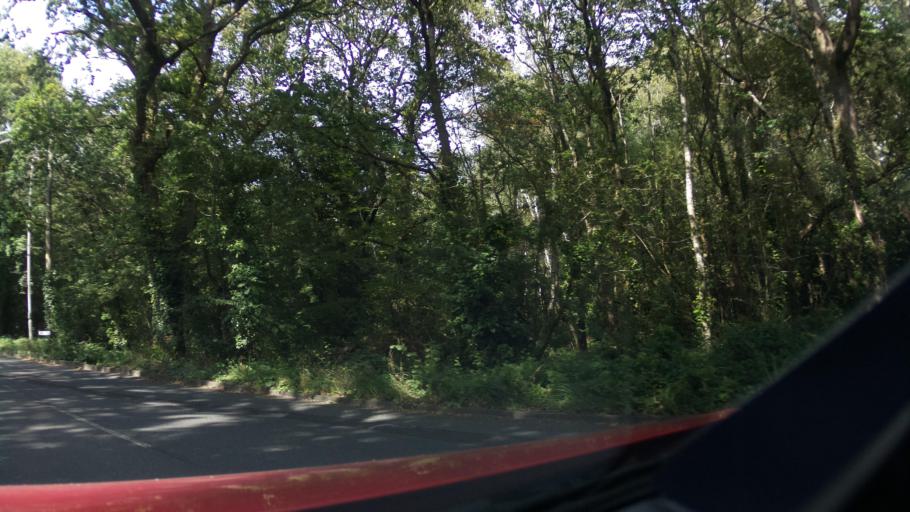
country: GB
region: England
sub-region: Hampshire
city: New Milton
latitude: 50.7464
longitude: -1.6883
